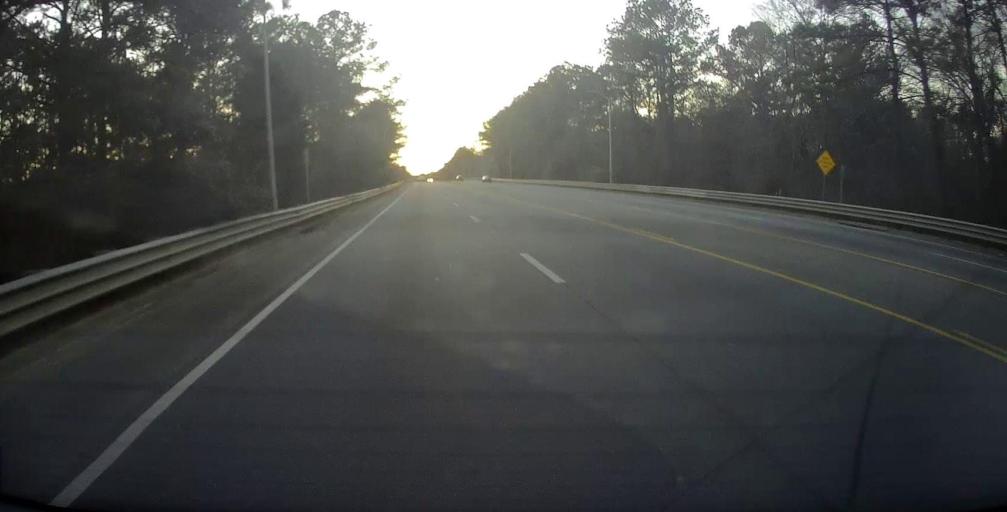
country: US
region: Georgia
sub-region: Dougherty County
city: Albany
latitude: 31.5523
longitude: -84.1427
